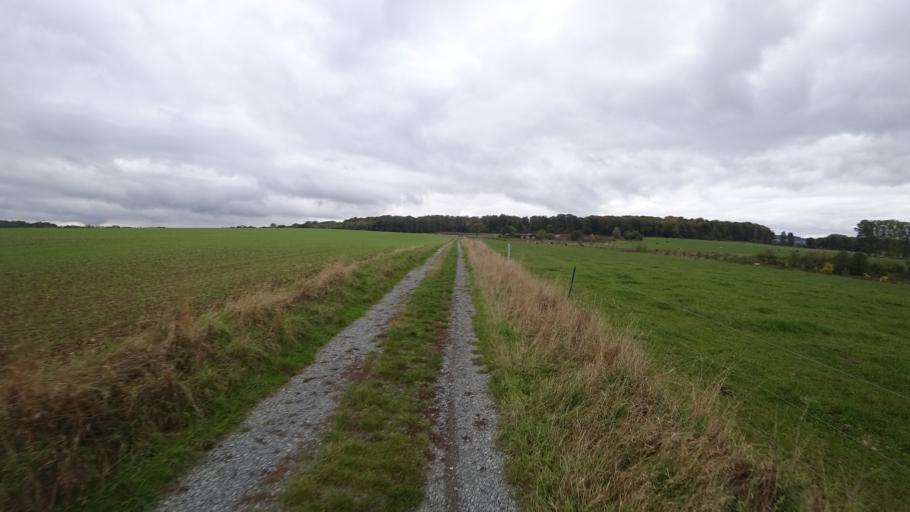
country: DE
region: Rheinland-Pfalz
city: Maxsain
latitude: 50.5448
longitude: 7.7718
